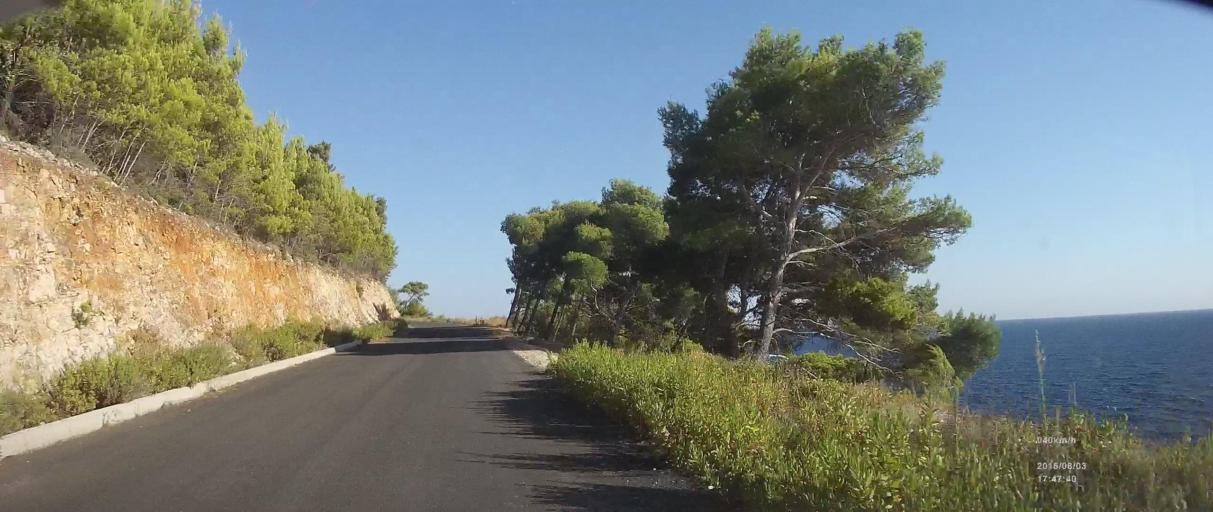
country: HR
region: Dubrovacko-Neretvanska
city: Blato
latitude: 42.7367
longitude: 17.5032
